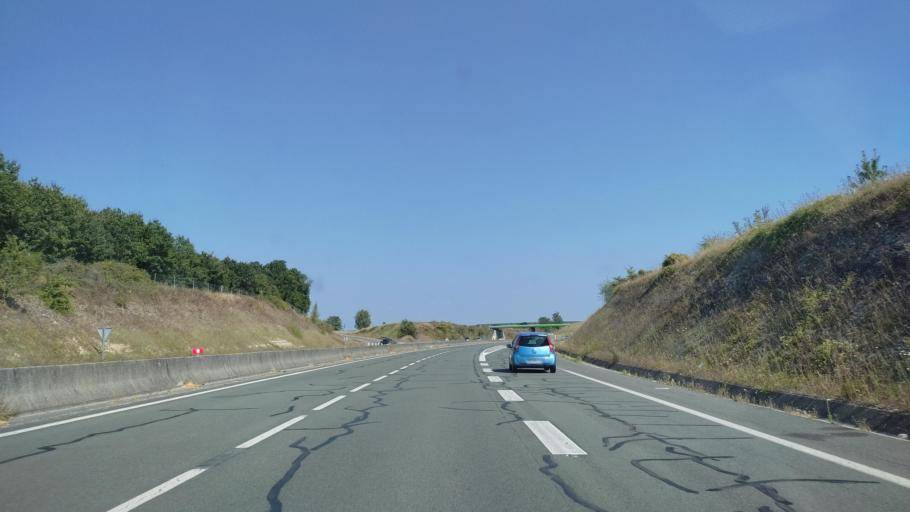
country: FR
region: Poitou-Charentes
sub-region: Departement de la Charente
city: Saint-Yrieix-sur-Charente
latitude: 45.6801
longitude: 0.1289
